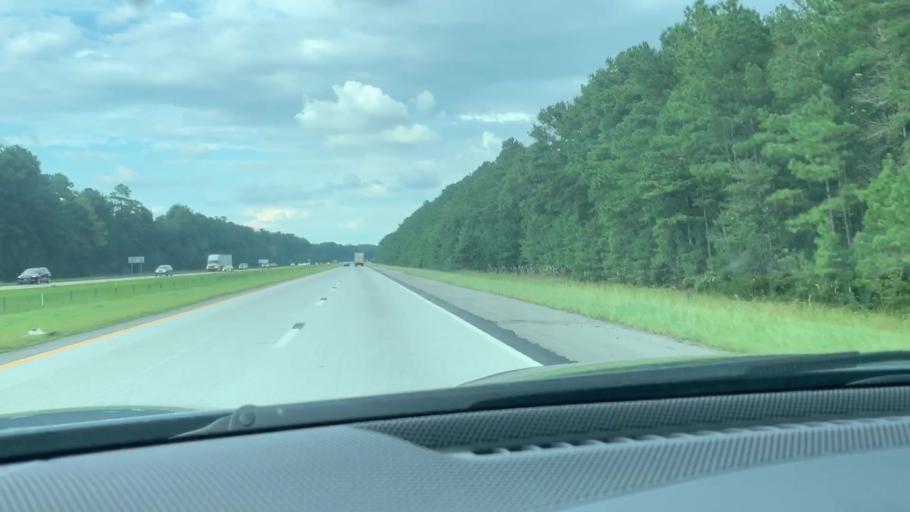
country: US
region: South Carolina
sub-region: Dorchester County
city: Saint George
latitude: 33.3010
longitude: -80.5558
